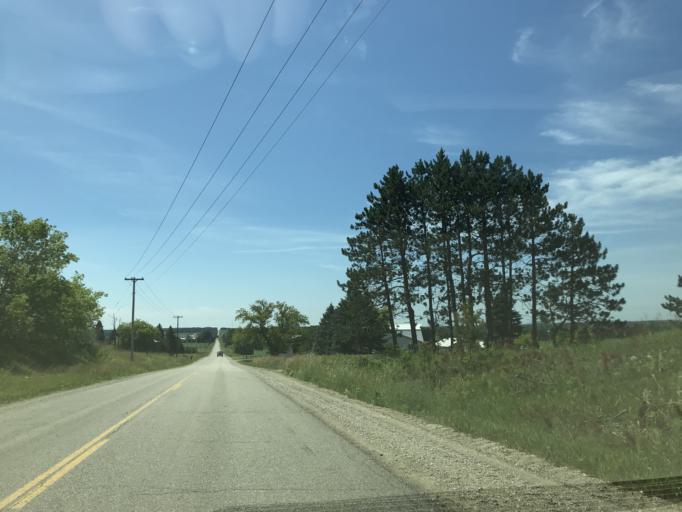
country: US
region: Michigan
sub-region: Missaukee County
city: Lake City
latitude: 44.3330
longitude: -85.0751
